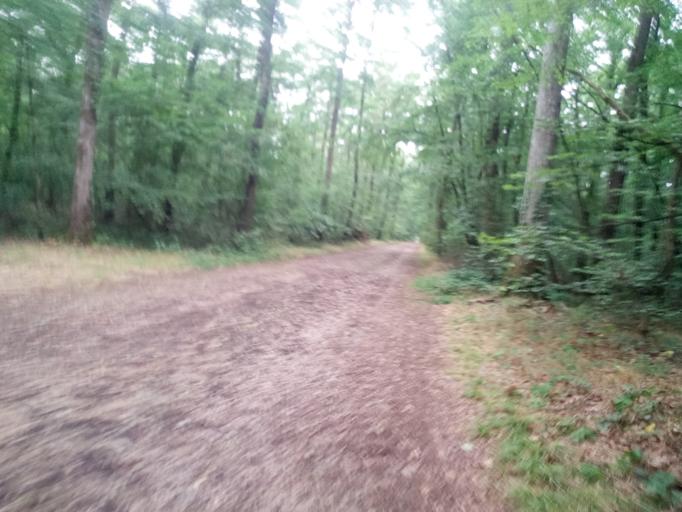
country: FR
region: Lower Normandy
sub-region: Departement du Calvados
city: Clinchamps-sur-Orne
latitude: 49.0440
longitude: -0.4300
